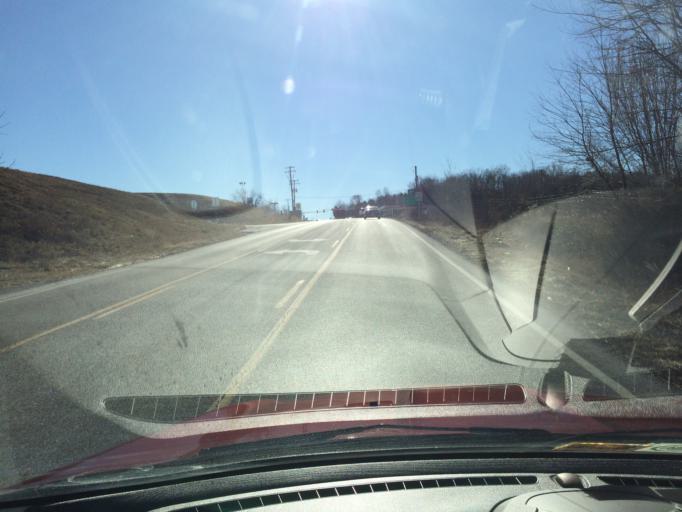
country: US
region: Virginia
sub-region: Augusta County
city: Weyers Cave
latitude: 38.2916
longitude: -78.9355
